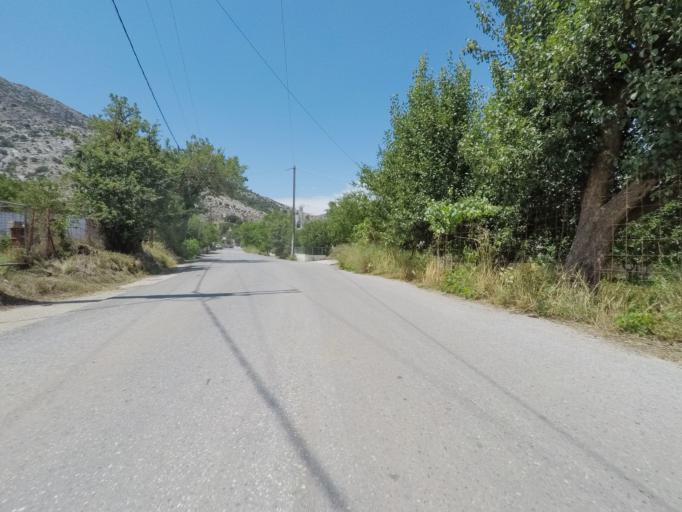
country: GR
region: Crete
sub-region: Nomos Irakleiou
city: Mokhos
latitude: 35.1837
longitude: 25.4330
